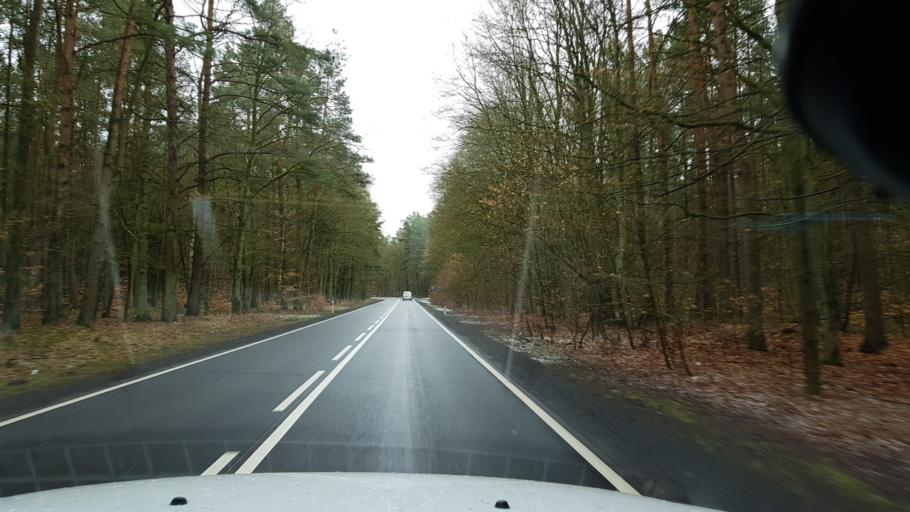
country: PL
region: West Pomeranian Voivodeship
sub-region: Powiat goleniowski
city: Stepnica
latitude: 53.6380
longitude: 14.6610
